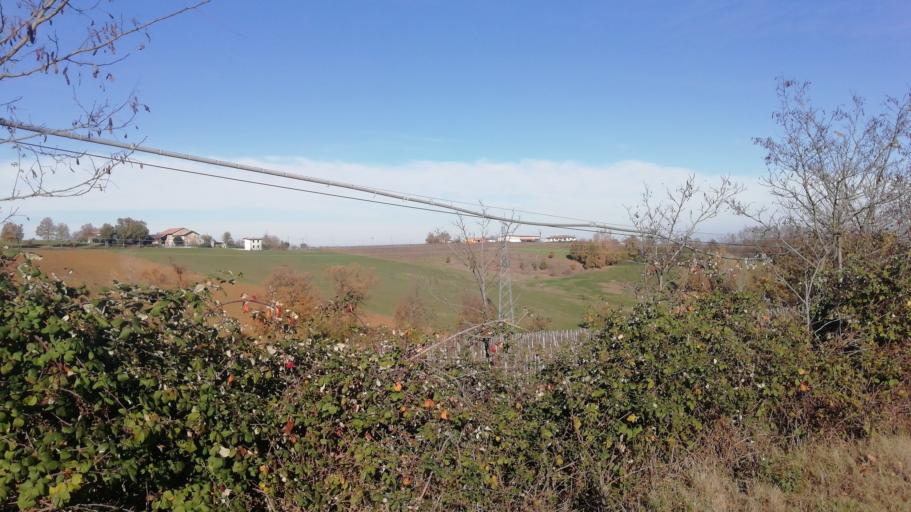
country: IT
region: Emilia-Romagna
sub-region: Provincia di Piacenza
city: Pianello Val Tidone
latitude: 44.9747
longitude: 9.4302
